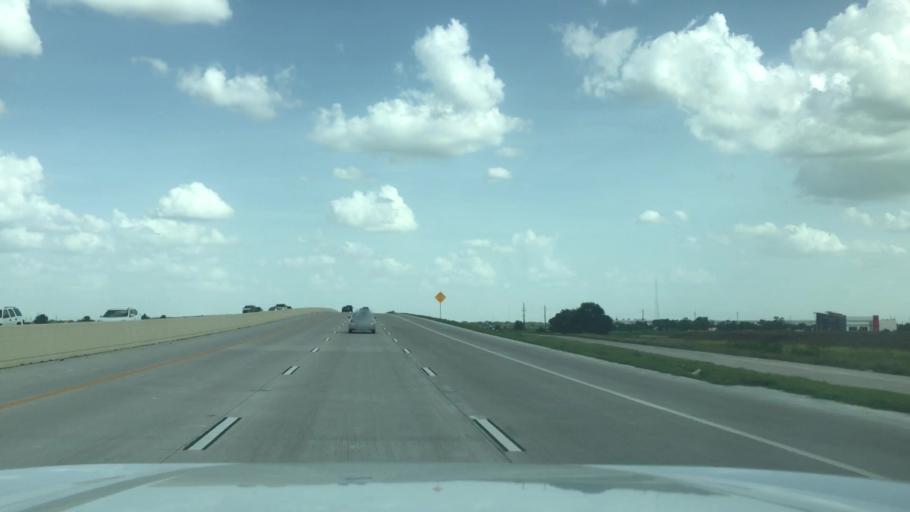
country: US
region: Texas
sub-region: Waller County
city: Waller
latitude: 30.0498
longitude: -95.8776
